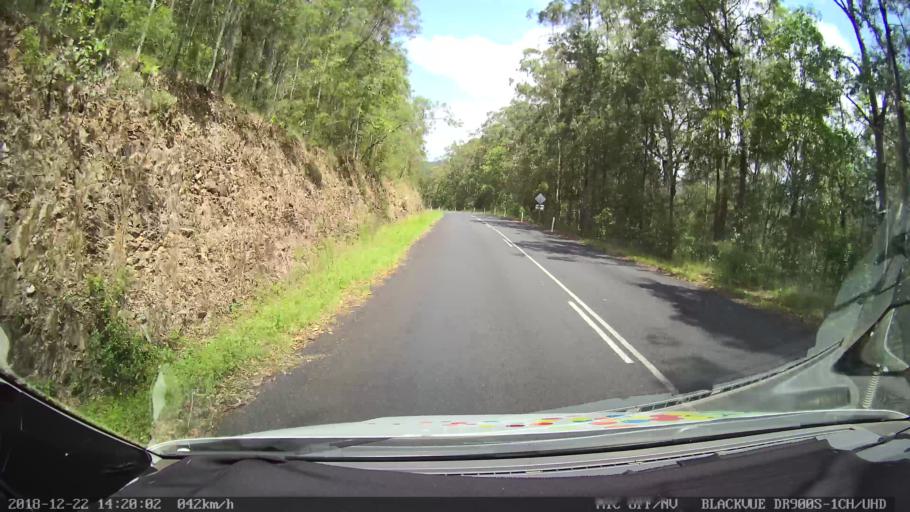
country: AU
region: New South Wales
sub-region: Clarence Valley
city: Coutts Crossing
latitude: -30.0119
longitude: 152.6599
